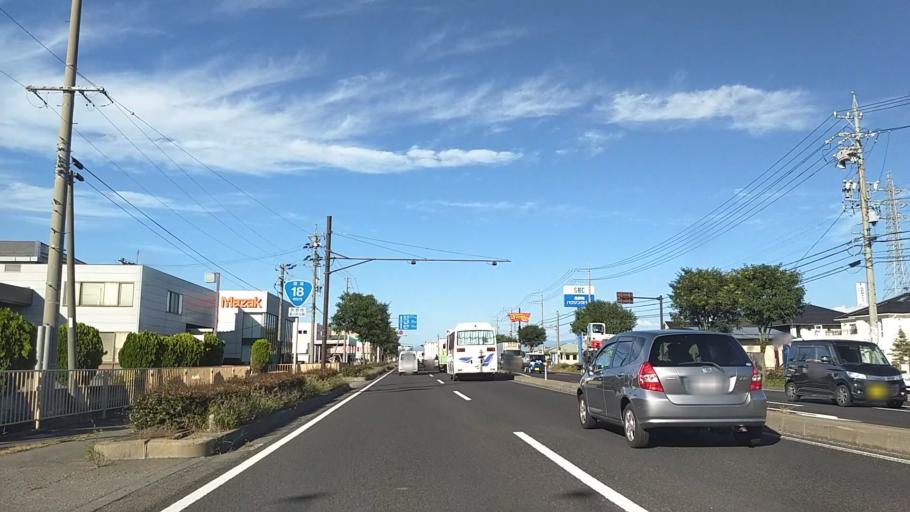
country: JP
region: Nagano
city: Nagano-shi
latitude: 36.5753
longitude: 138.1560
